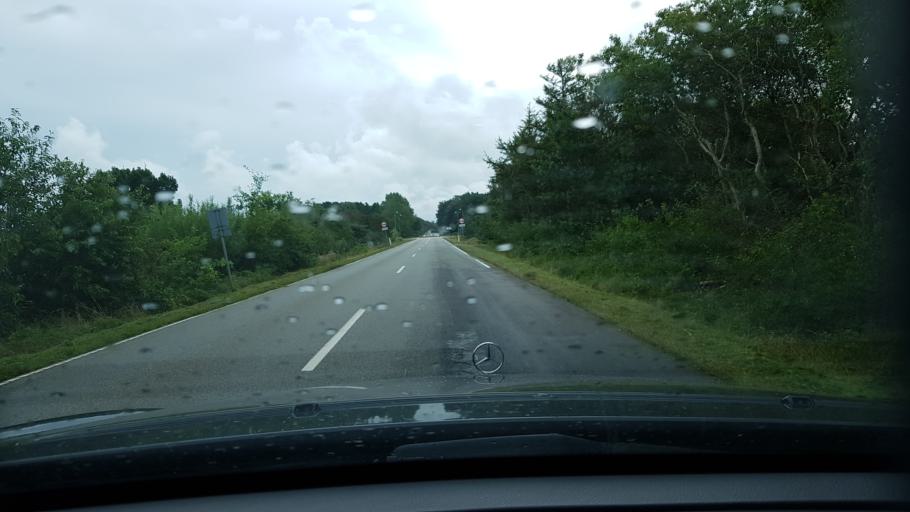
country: DK
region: North Denmark
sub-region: Alborg Kommune
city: Hals
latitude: 56.8222
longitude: 10.2693
